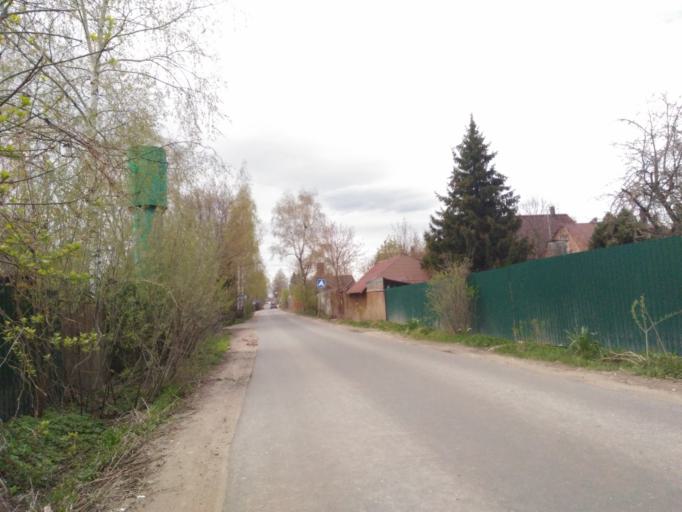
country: RU
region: Moskovskaya
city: Nakhabino
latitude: 55.8495
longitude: 37.1494
